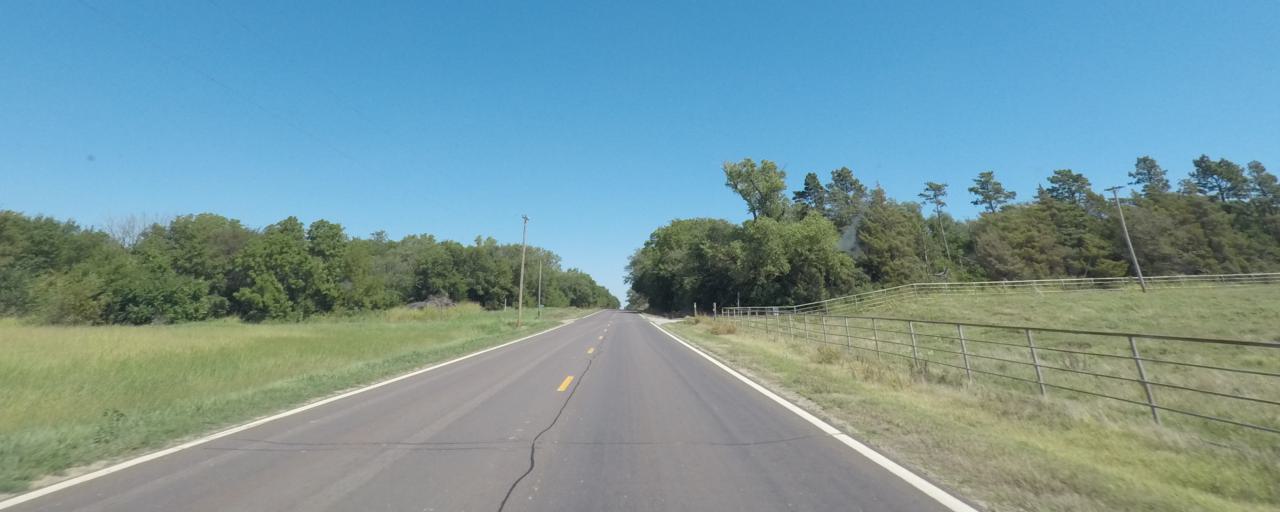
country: US
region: Kansas
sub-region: Sumner County
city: Wellington
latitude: 37.0707
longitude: -97.4014
